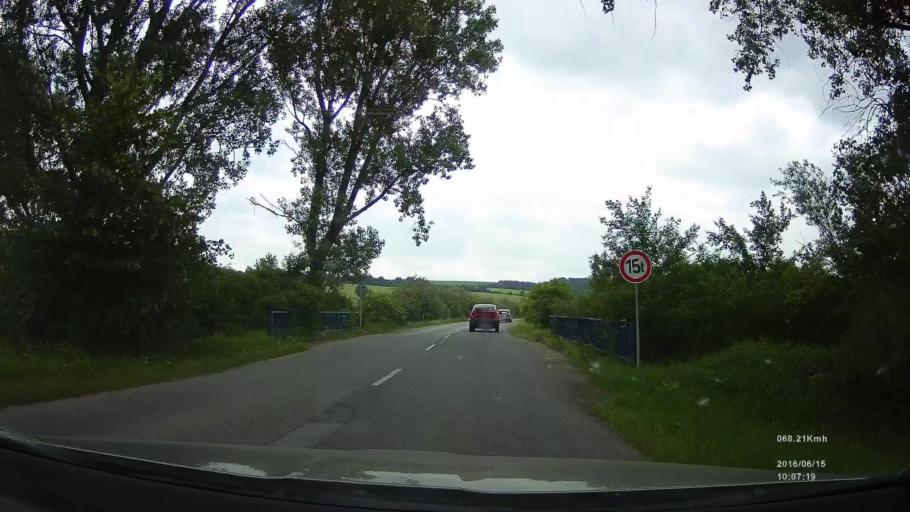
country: SK
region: Kosicky
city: Kosice
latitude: 48.7782
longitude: 21.3281
